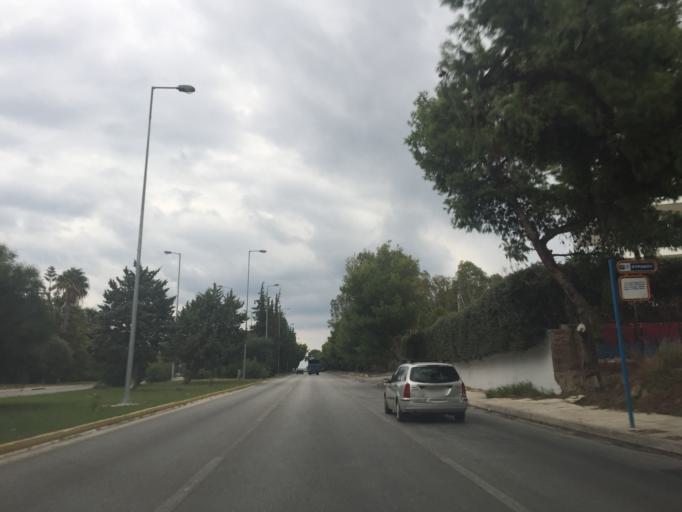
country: GR
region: Attica
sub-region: Nomarchia Anatolikis Attikis
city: Vouliagmeni
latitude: 37.8251
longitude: 23.7744
